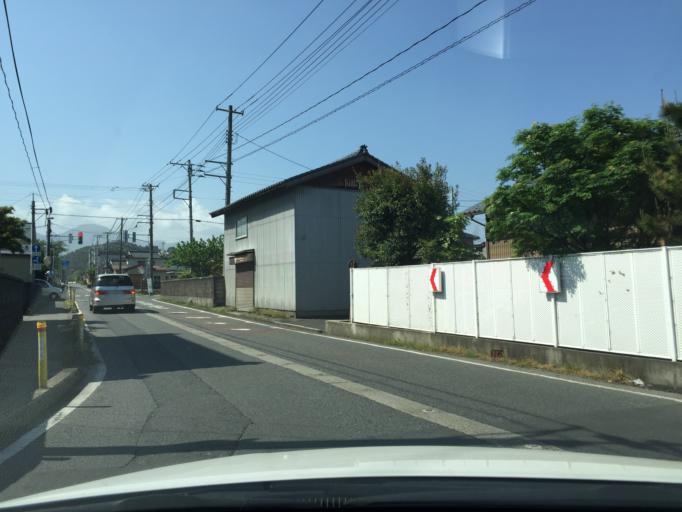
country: JP
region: Niigata
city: Muramatsu
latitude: 37.6996
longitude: 139.1891
